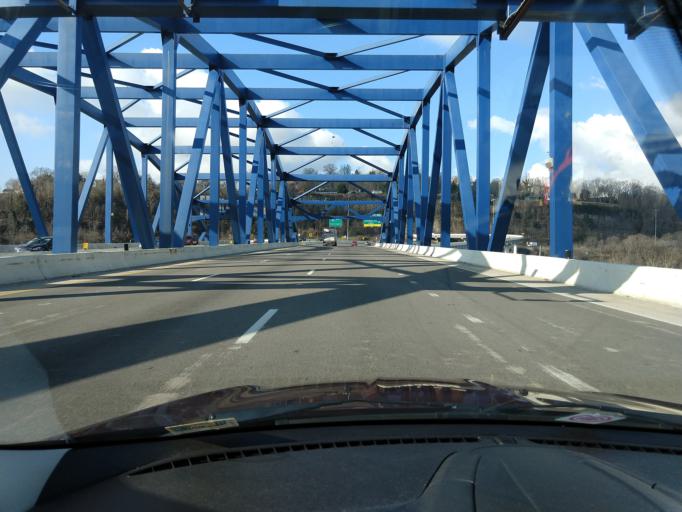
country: US
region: West Virginia
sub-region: Kanawha County
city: Charleston
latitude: 38.3573
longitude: -81.6481
